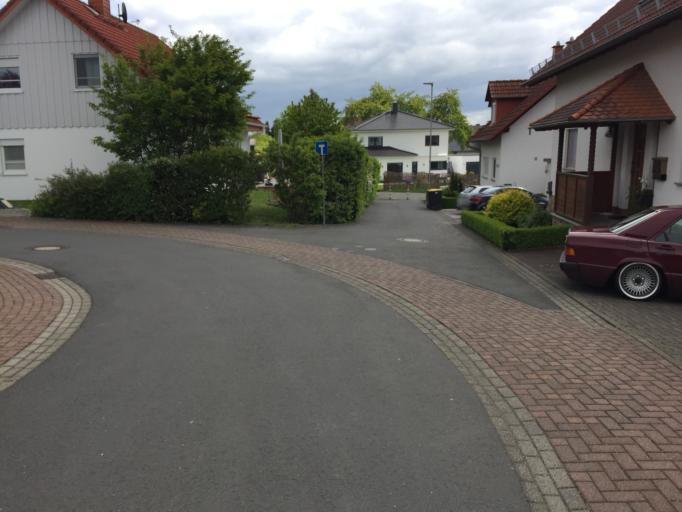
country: DE
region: Hesse
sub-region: Regierungsbezirk Giessen
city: Grunberg
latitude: 50.5770
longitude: 8.9336
